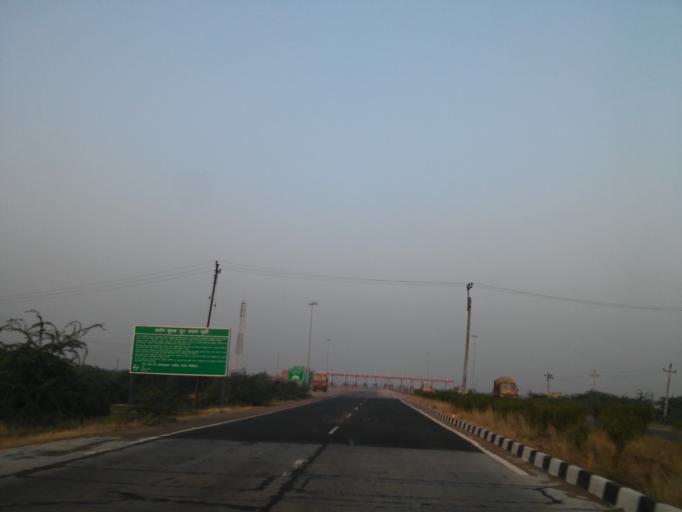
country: IN
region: Gujarat
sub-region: Rajkot
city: Morbi
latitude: 23.0363
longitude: 70.9315
